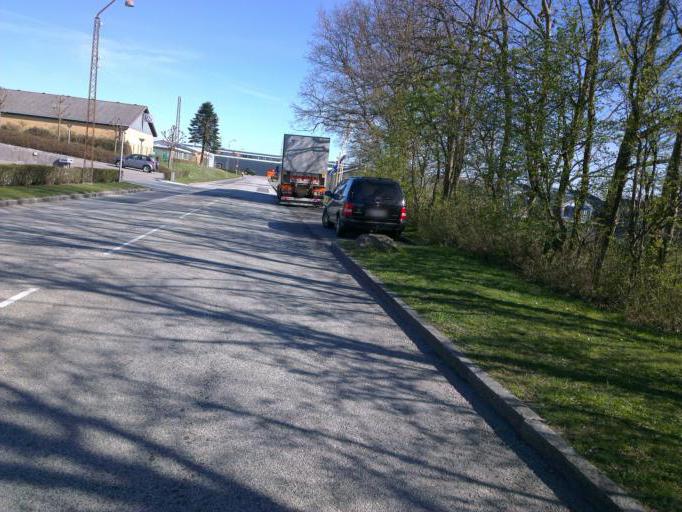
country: DK
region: Capital Region
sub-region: Frederikssund Kommune
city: Frederikssund
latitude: 55.8456
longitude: 12.0706
